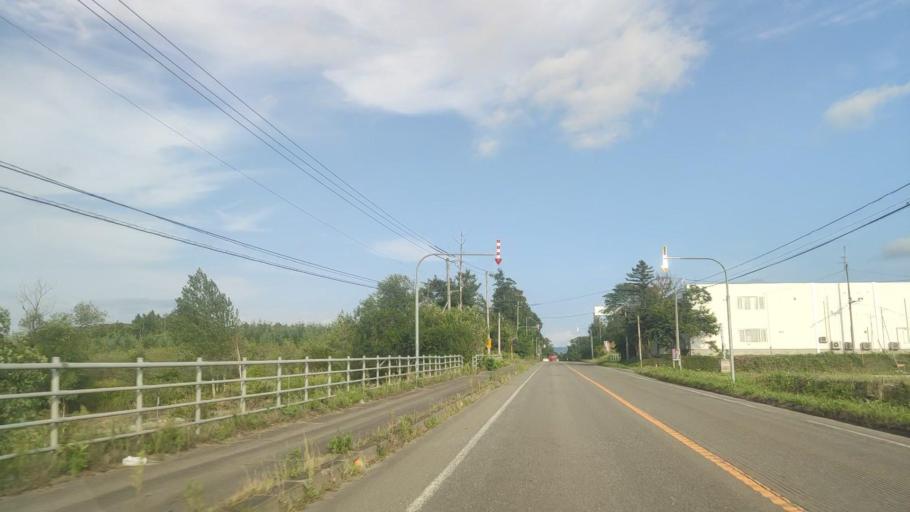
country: JP
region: Hokkaido
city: Iwamizawa
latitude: 43.0255
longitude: 141.8426
